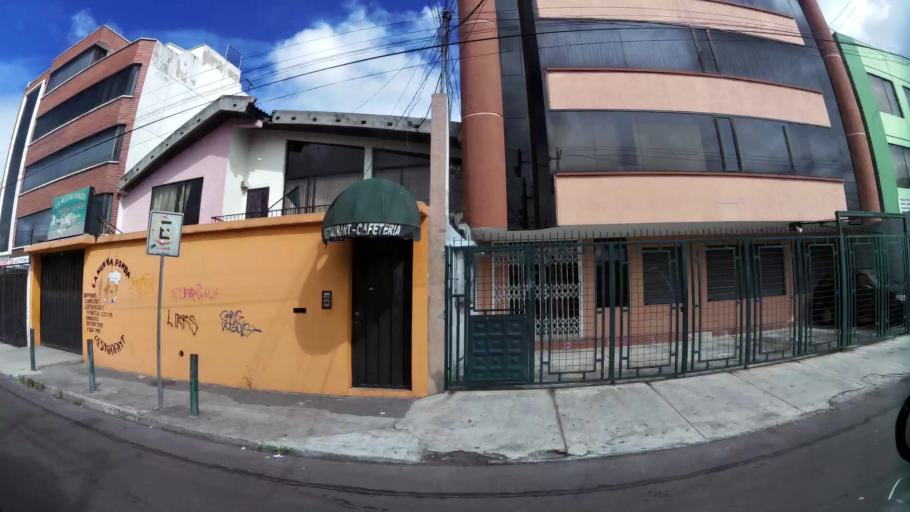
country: EC
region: Pichincha
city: Quito
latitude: -0.1547
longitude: -78.4781
